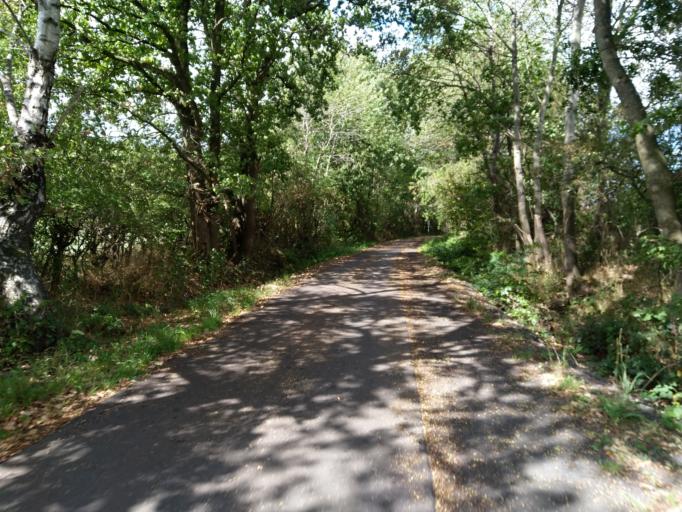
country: BE
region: Wallonia
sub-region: Province de Liege
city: Aubel
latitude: 50.6695
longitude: 5.8569
